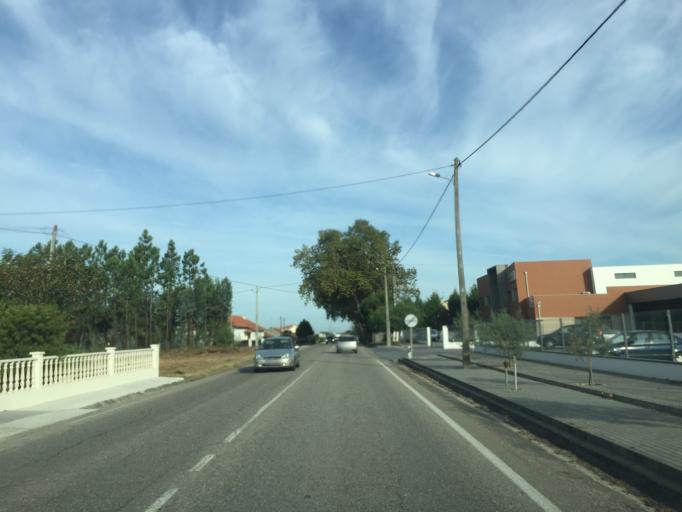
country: PT
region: Leiria
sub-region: Pombal
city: Lourical
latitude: 39.9622
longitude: -8.7893
